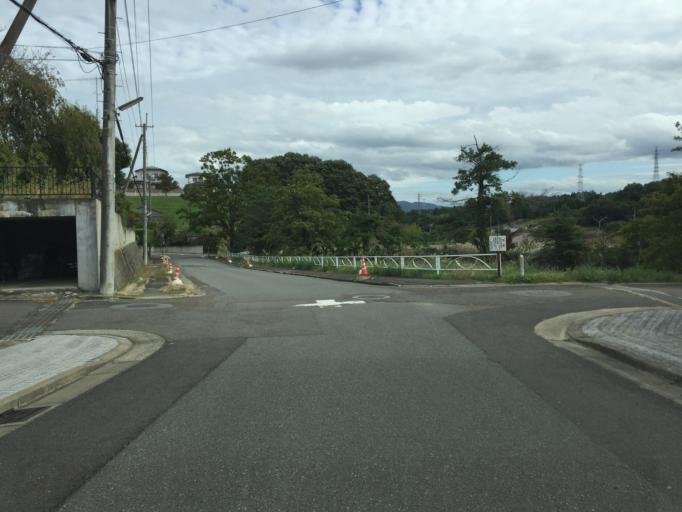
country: JP
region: Fukushima
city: Fukushima-shi
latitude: 37.6913
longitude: 140.4800
